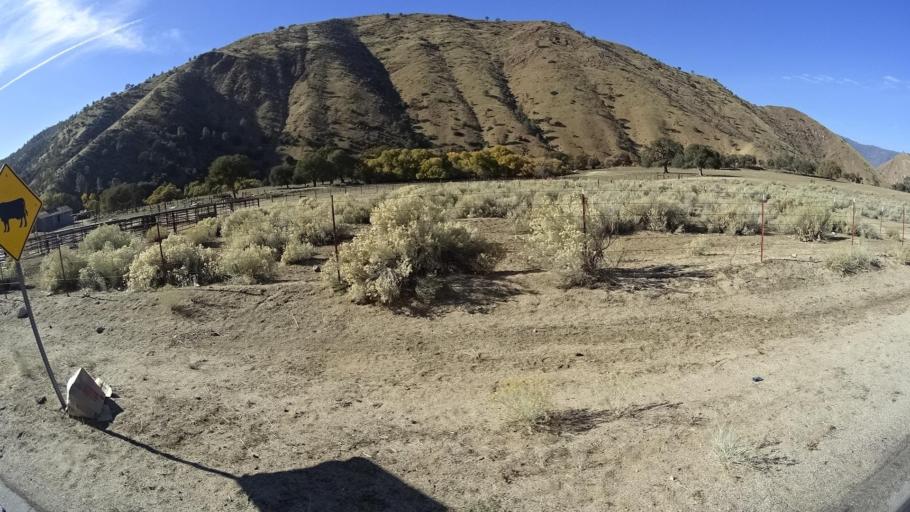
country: US
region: California
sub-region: Kern County
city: Bodfish
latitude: 35.5380
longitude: -118.5100
